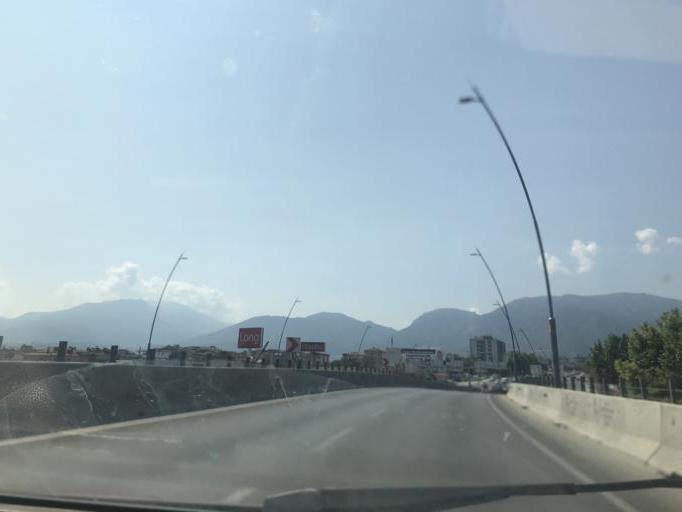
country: TR
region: Denizli
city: Denizli
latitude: 37.7821
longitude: 29.0965
